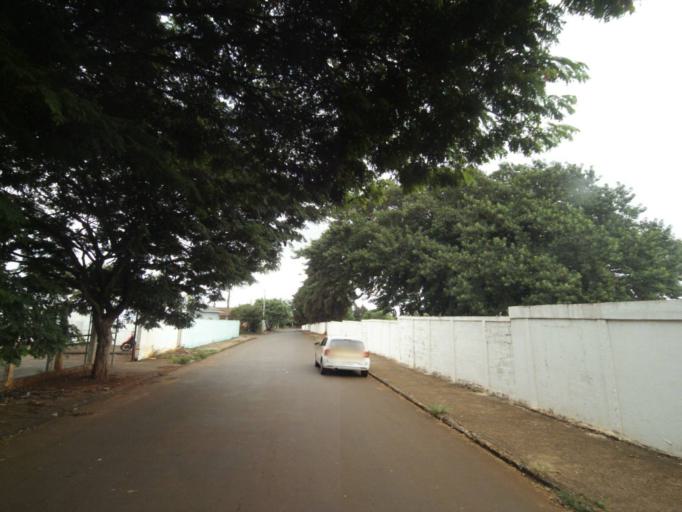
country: BR
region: Parana
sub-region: Campo Mourao
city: Campo Mourao
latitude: -24.0237
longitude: -52.3614
